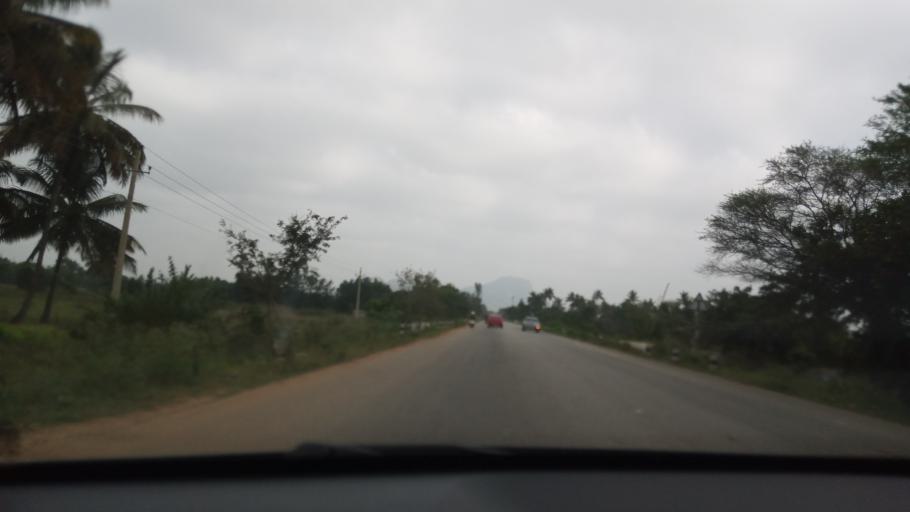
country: IN
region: Karnataka
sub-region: Chikkaballapur
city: Chintamani
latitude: 13.3057
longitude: 77.9740
